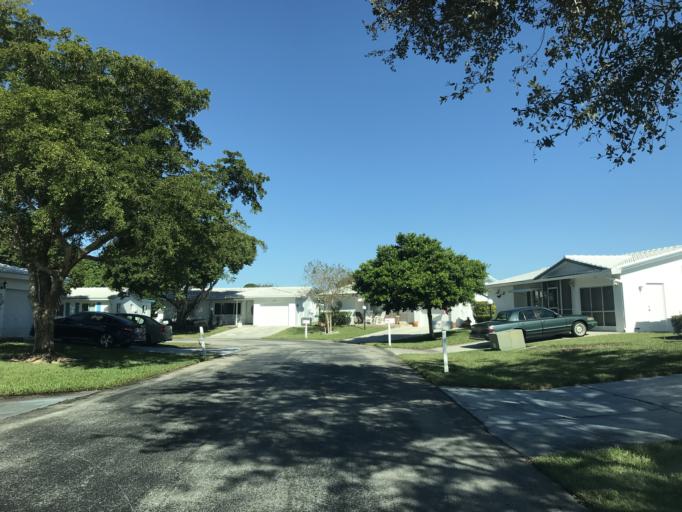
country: US
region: Florida
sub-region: Broward County
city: Plantation
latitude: 26.1379
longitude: -80.2675
